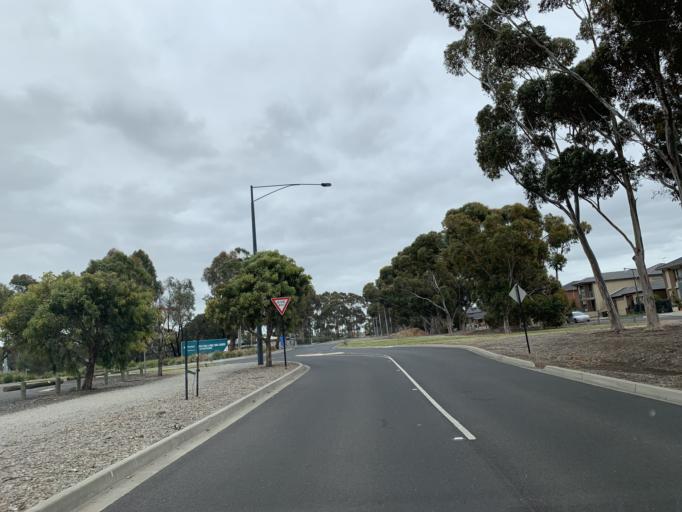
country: AU
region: Victoria
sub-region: Brimbank
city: St Albans
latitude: -37.7544
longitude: 144.8000
